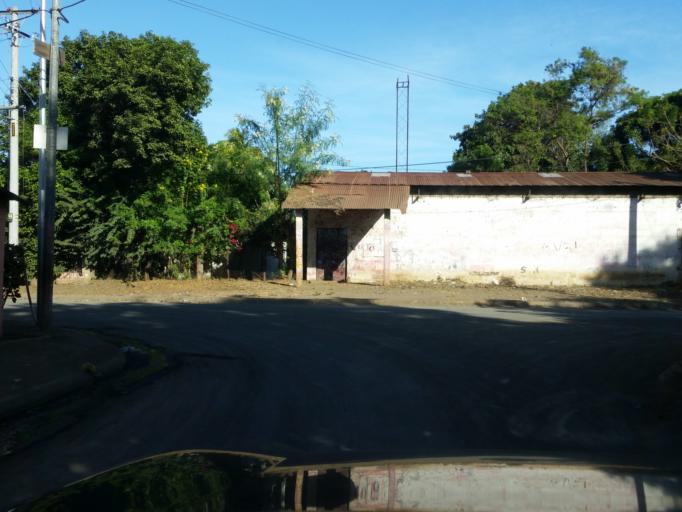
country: NI
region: Masaya
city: Ticuantepe
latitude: 12.0661
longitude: -86.2301
